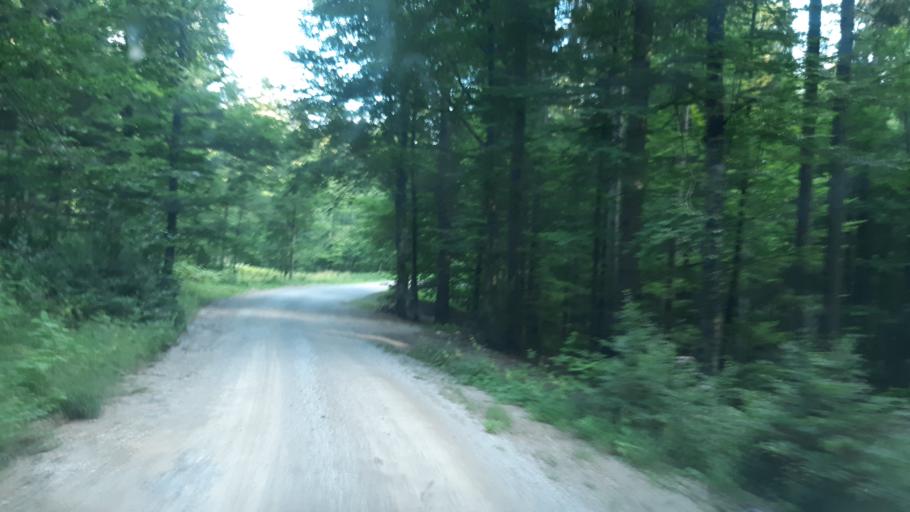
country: SI
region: Kocevje
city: Kocevje
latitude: 45.6719
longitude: 14.9716
